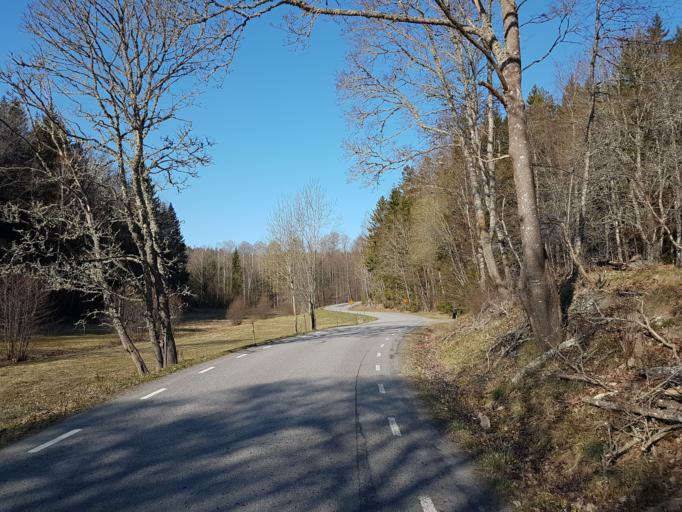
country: SE
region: OEstergoetland
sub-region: Valdemarsviks Kommun
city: Gusum
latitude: 58.1885
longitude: 16.3047
